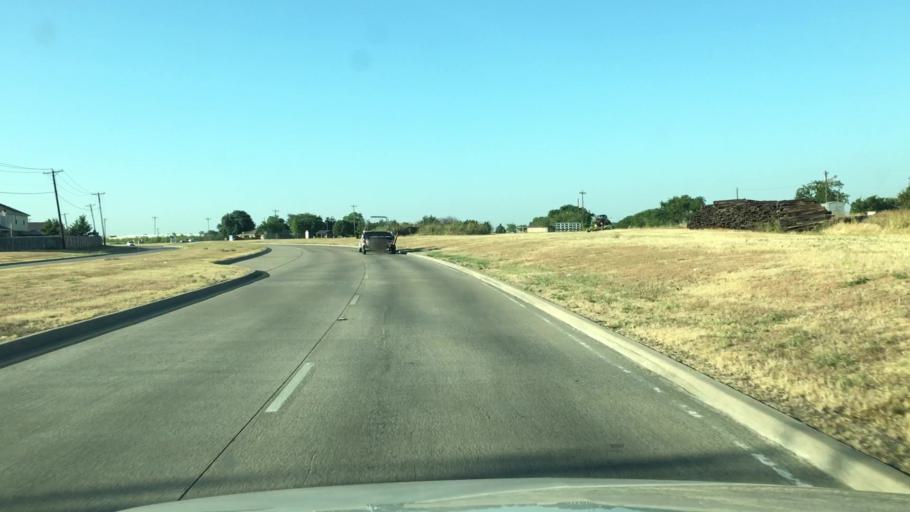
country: US
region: Texas
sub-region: Tarrant County
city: Crowley
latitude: 32.5458
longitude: -97.3659
